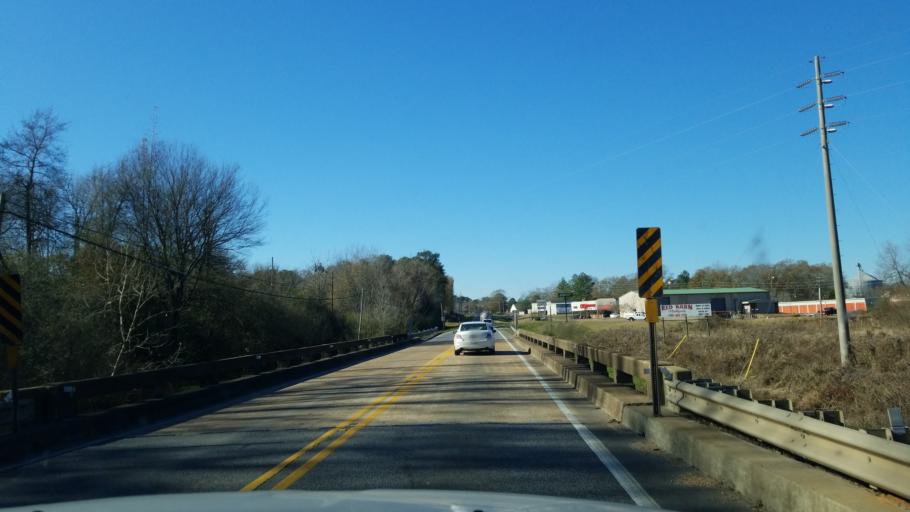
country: US
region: Alabama
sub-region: Pickens County
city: Gordo
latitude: 33.3147
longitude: -87.8978
